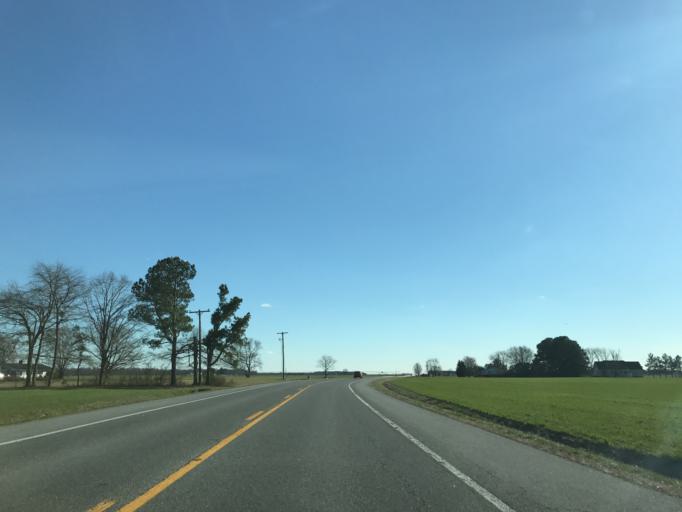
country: US
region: Maryland
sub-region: Caroline County
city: Greensboro
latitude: 39.1362
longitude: -75.8640
